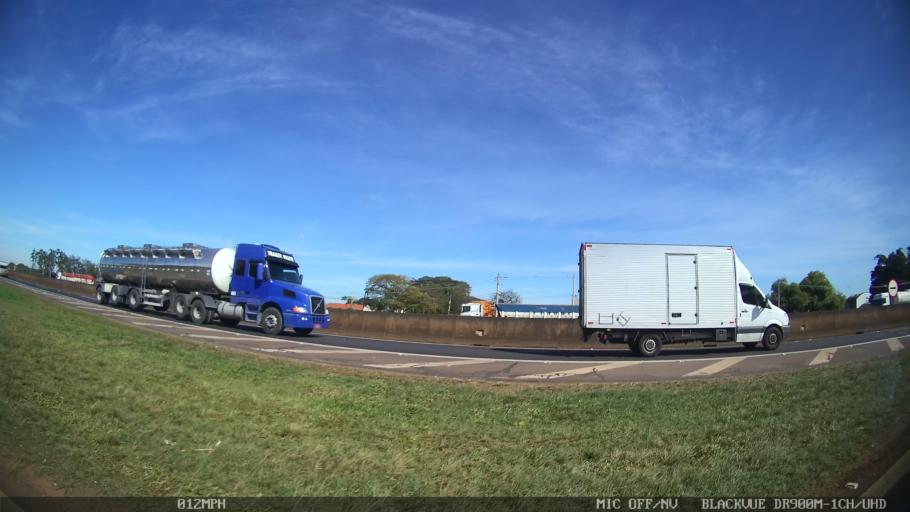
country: BR
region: Sao Paulo
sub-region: Leme
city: Leme
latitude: -22.2015
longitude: -47.3956
